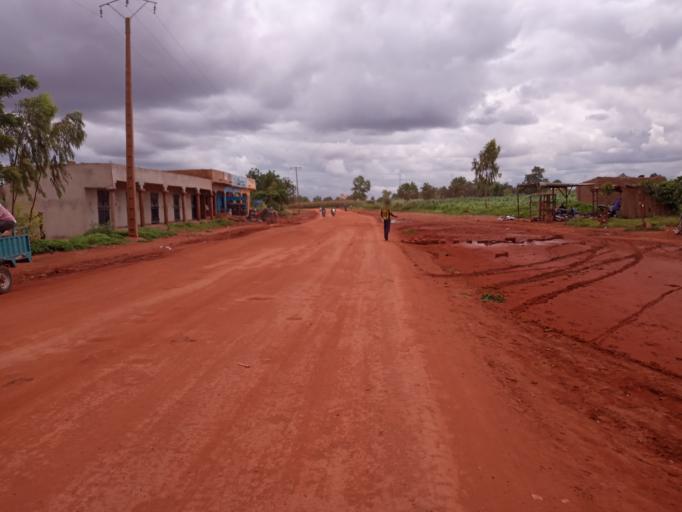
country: ML
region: Bamako
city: Bamako
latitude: 12.5426
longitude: -7.9942
